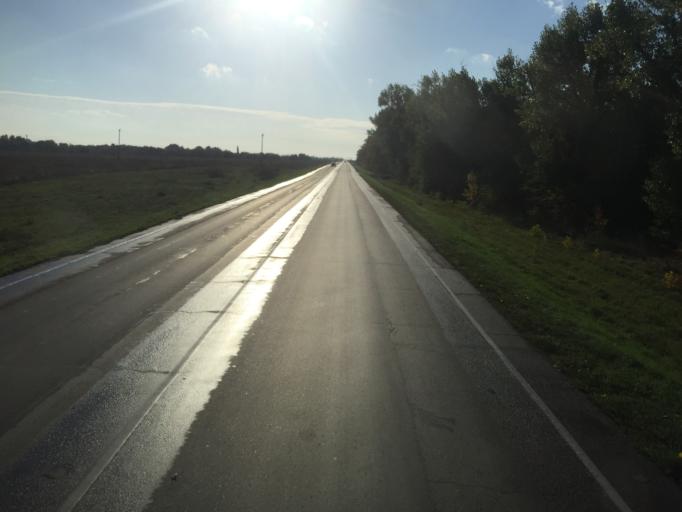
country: RU
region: Rostov
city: Mechetinskaya
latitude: 46.6641
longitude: 40.5466
